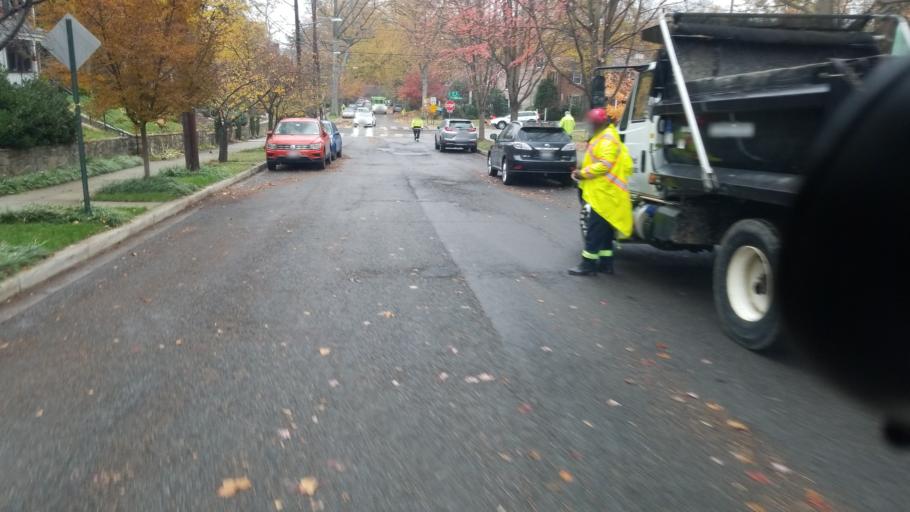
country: US
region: Maryland
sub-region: Montgomery County
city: Friendship Village
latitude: 38.9423
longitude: -77.0735
